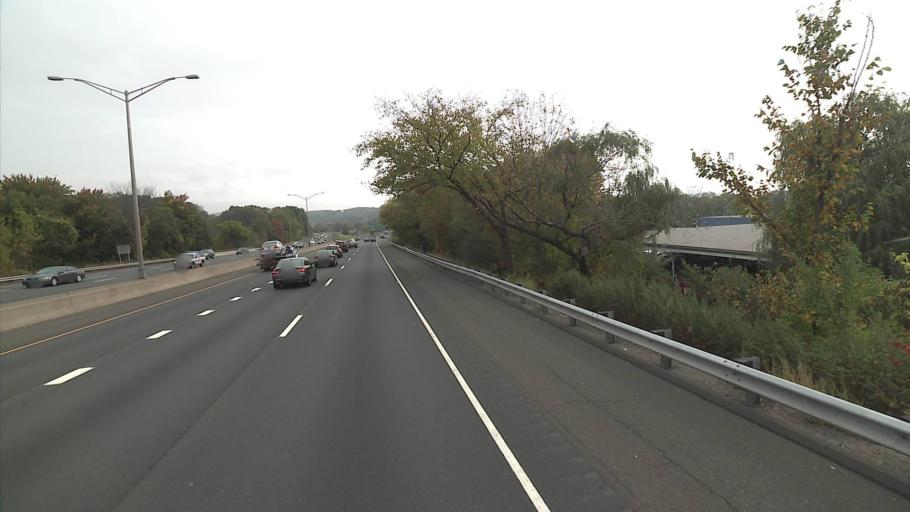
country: US
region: Connecticut
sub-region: Fairfield County
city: Danbury
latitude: 41.4161
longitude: -73.4324
